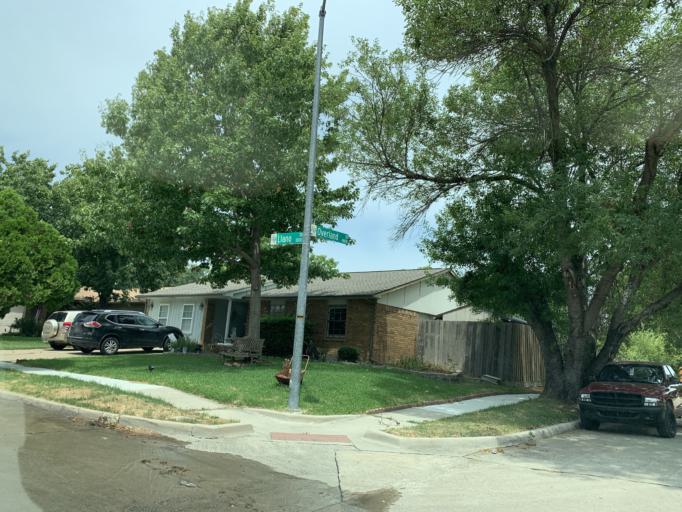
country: US
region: Texas
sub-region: Dallas County
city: Cedar Hill
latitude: 32.6533
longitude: -97.0180
